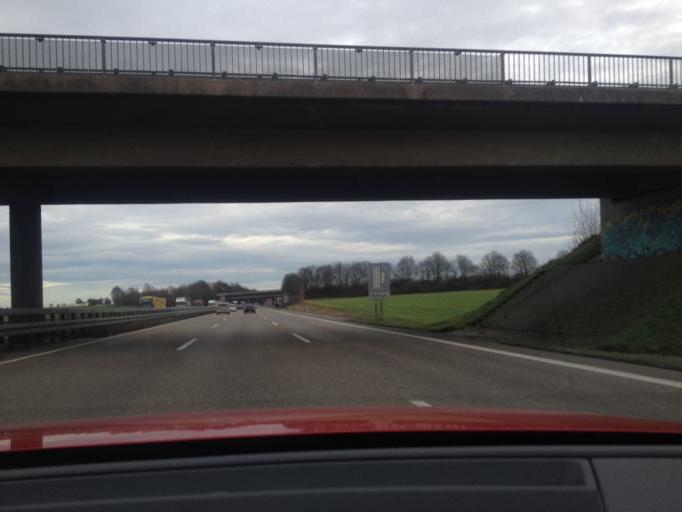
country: DE
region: Baden-Wuerttemberg
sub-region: Regierungsbezirk Stuttgart
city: Neuenstein
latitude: 49.2145
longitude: 9.6041
